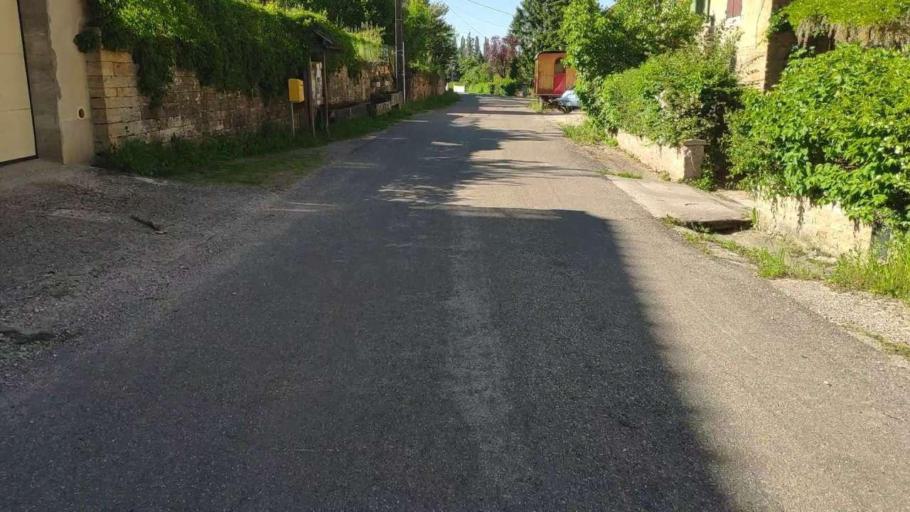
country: FR
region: Franche-Comte
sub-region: Departement du Jura
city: Montmorot
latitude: 46.7212
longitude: 5.5517
